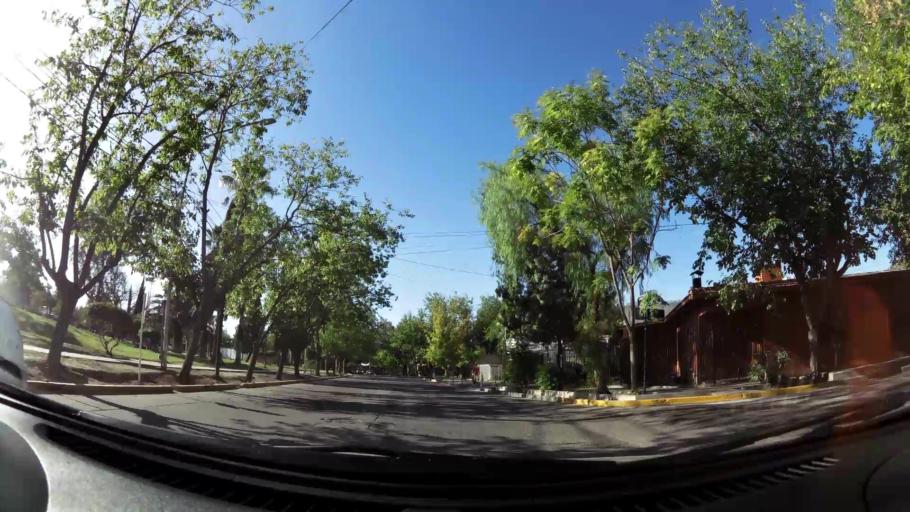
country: AR
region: Mendoza
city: Villa Nueva
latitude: -32.9060
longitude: -68.8002
